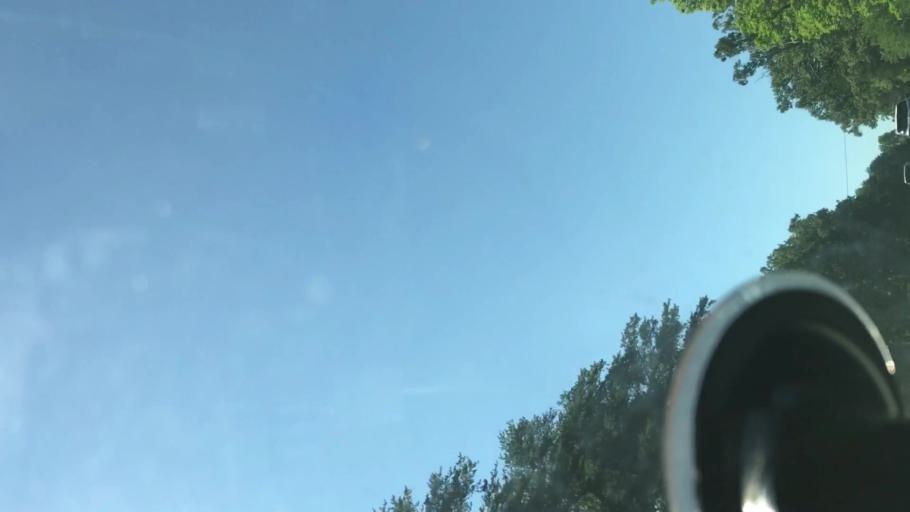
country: US
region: Virginia
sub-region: Spotsylvania County
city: Spotsylvania Courthouse
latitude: 38.1632
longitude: -77.5198
